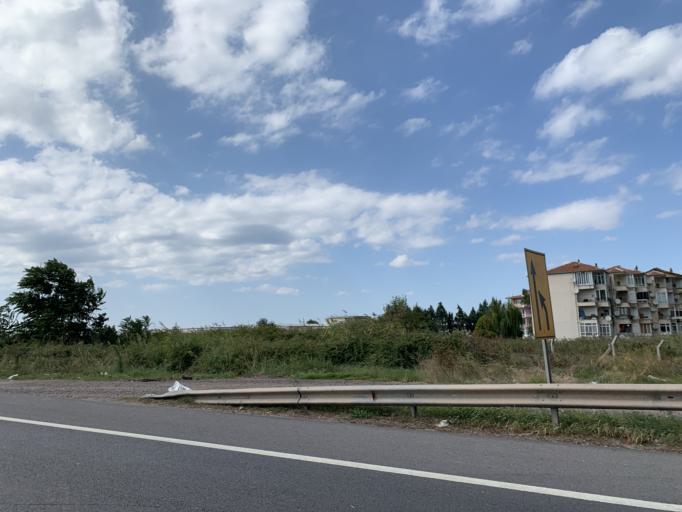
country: TR
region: Yalova
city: Taskopru
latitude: 40.6881
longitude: 29.4201
